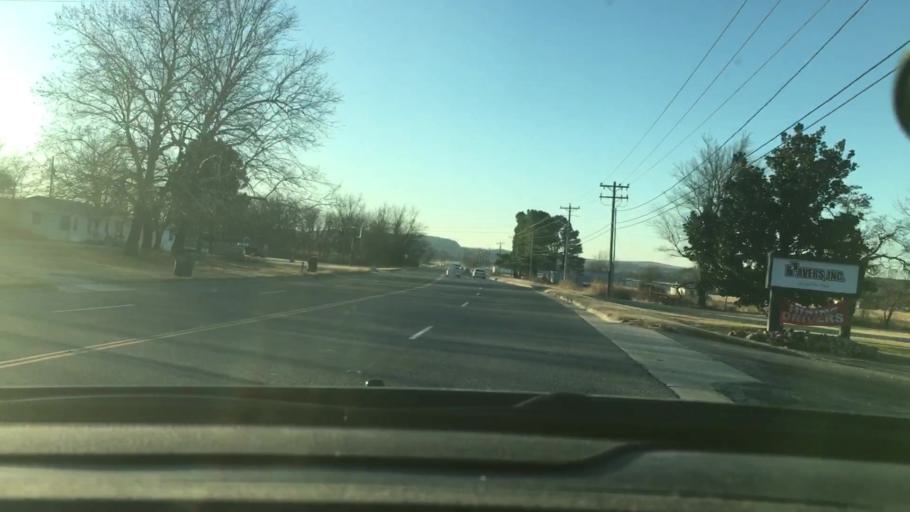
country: US
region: Oklahoma
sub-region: Murray County
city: Davis
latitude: 34.4745
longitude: -97.1318
